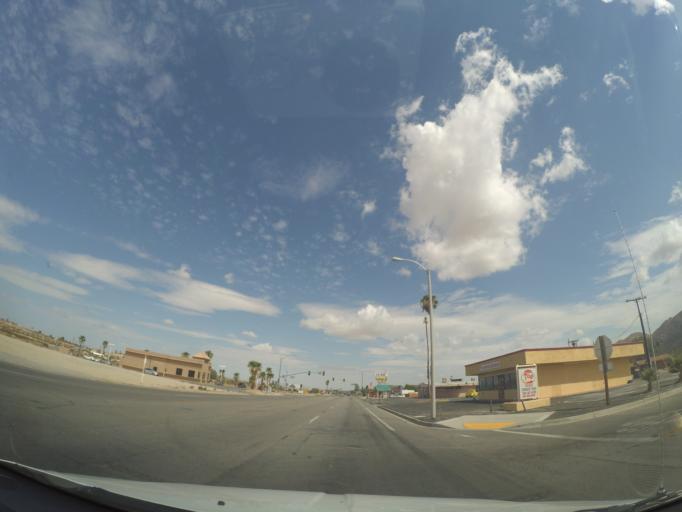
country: US
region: California
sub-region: San Bernardino County
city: Twentynine Palms
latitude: 34.1354
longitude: -116.0896
